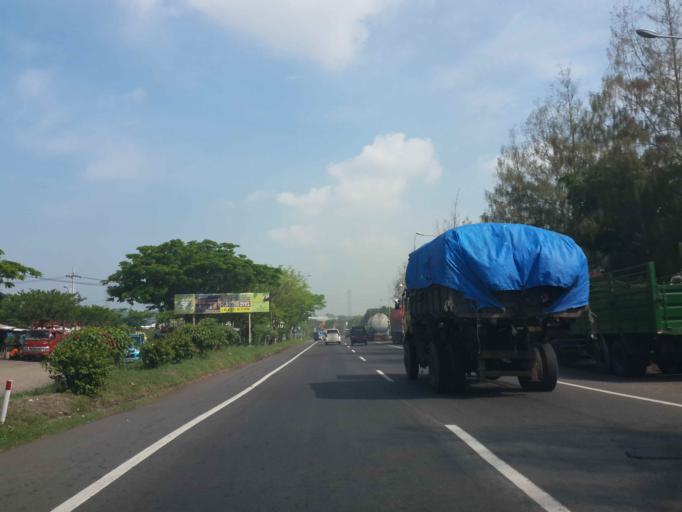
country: ID
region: East Java
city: Kebomas
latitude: -7.2003
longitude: 112.6458
